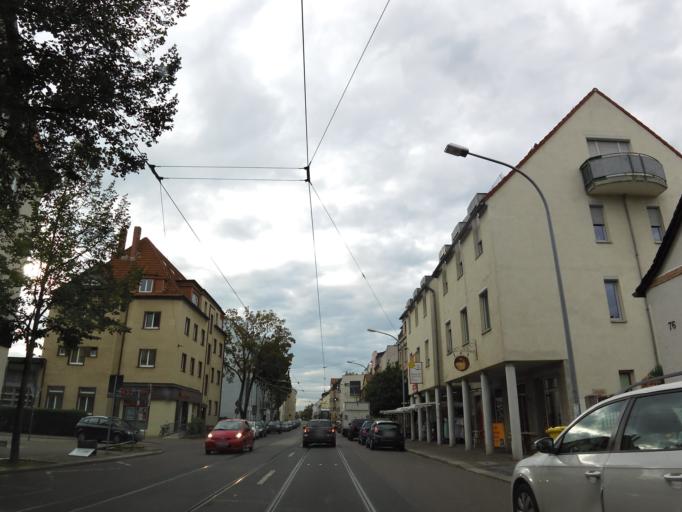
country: DE
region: Saxony
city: Schkeuditz
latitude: 51.3595
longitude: 12.2924
